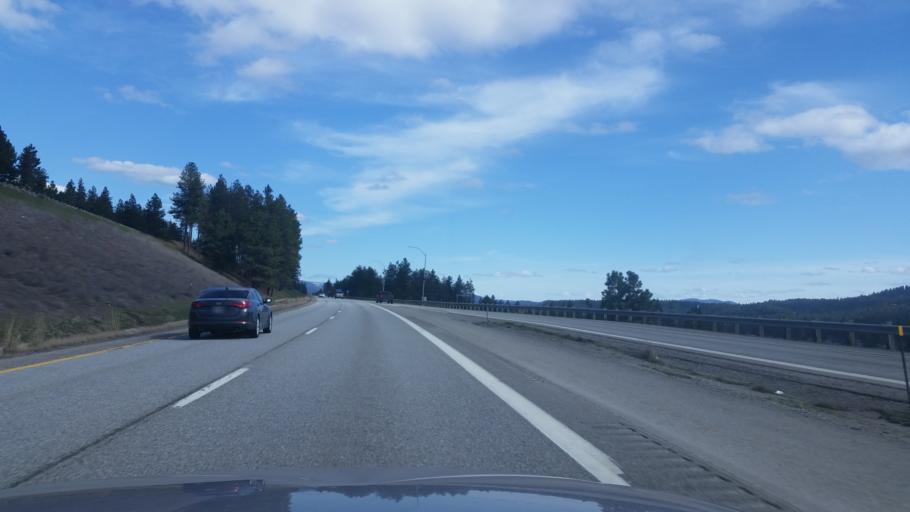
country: US
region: Idaho
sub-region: Kootenai County
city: Post Falls
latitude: 47.7090
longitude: -116.8885
